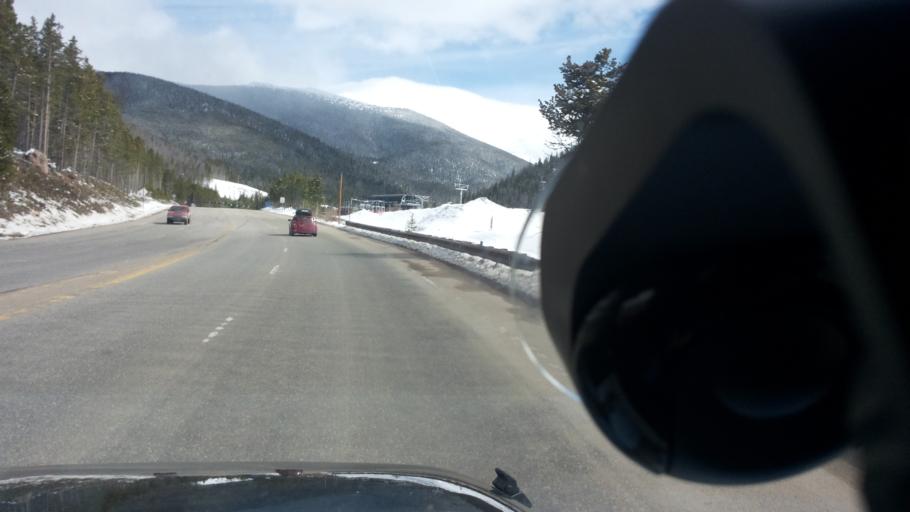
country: US
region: Colorado
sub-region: Grand County
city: Fraser
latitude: 39.8848
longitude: -105.7598
